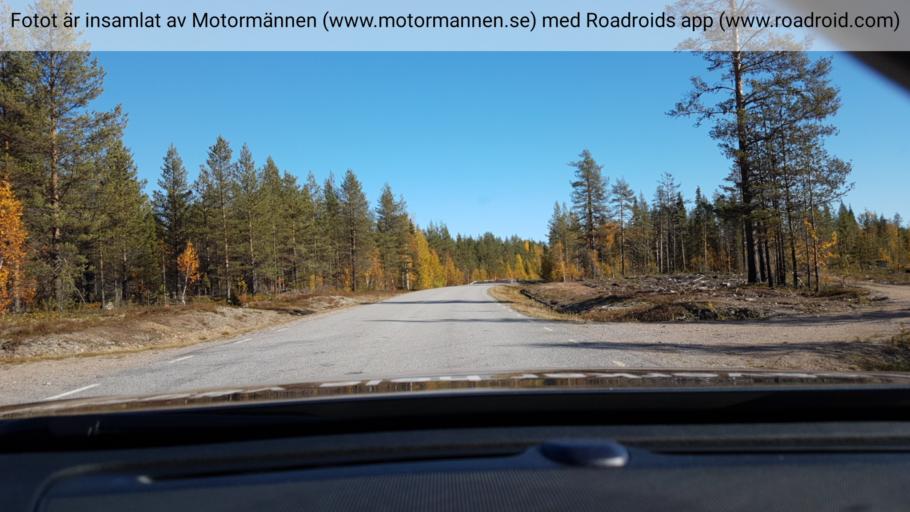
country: SE
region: Norrbotten
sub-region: Gallivare Kommun
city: Gaellivare
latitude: 66.4636
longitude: 20.8110
